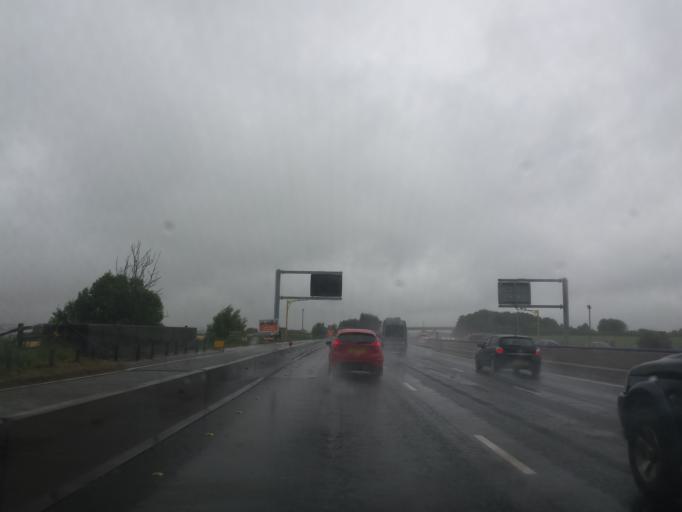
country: GB
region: England
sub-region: Derbyshire
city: Tibshelf
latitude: 53.1341
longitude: -1.3296
